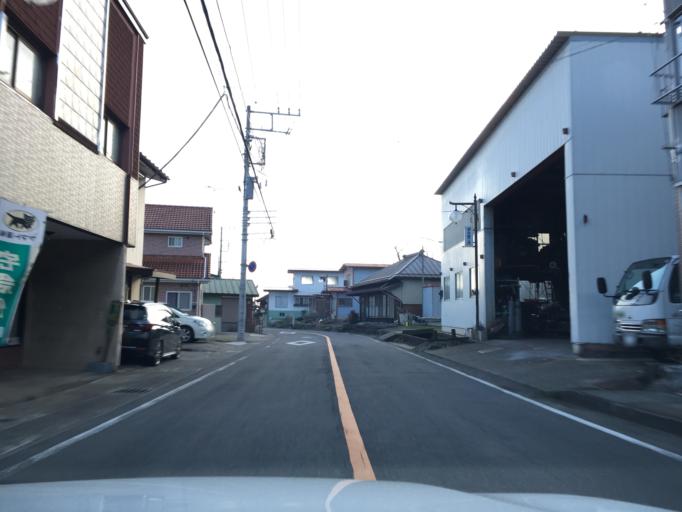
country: JP
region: Tochigi
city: Otawara
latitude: 36.8615
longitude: 140.1241
